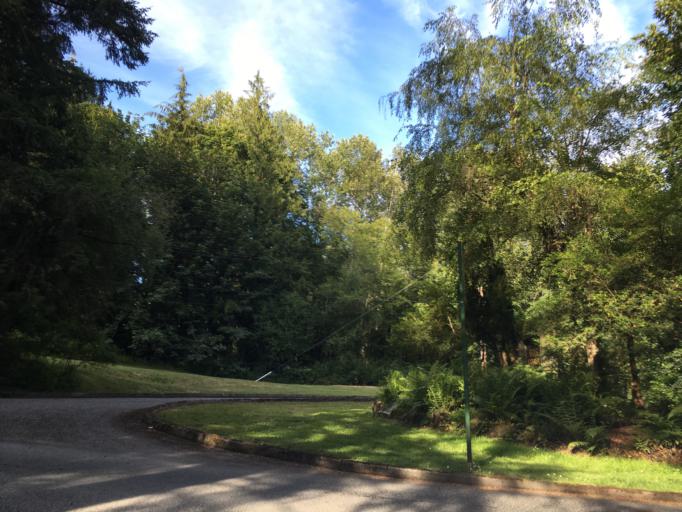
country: US
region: Washington
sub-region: Whatcom County
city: Geneva
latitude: 48.7056
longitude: -122.4468
